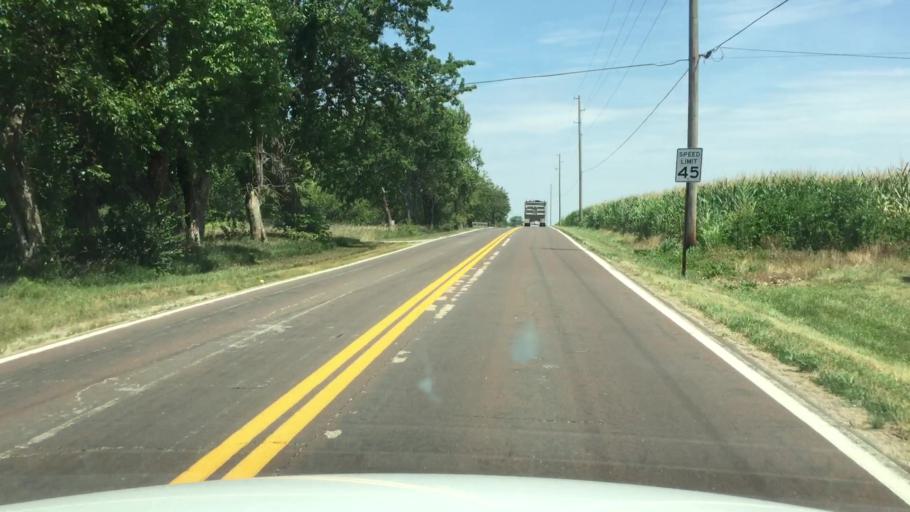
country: US
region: Kansas
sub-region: Shawnee County
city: Topeka
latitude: 38.9861
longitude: -95.5375
